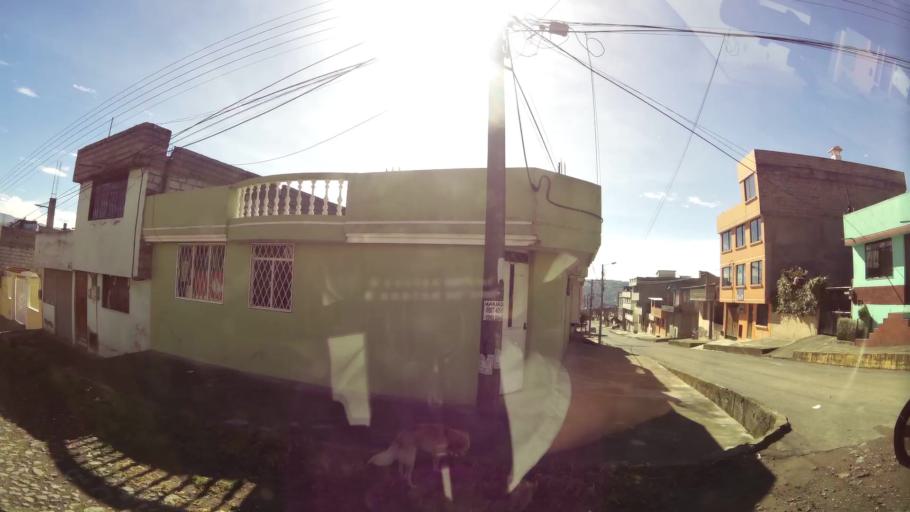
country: EC
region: Pichincha
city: Quito
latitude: -0.3054
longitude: -78.5679
